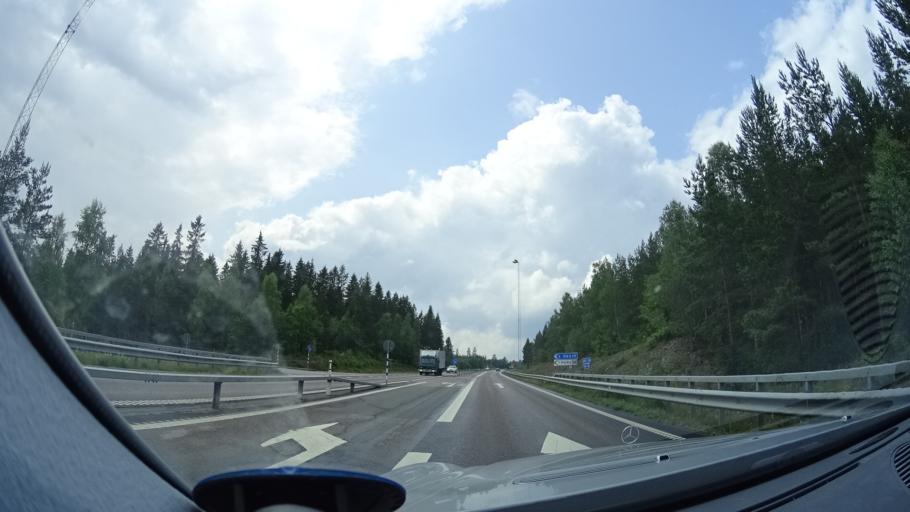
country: SE
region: Kalmar
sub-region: Nybro Kommun
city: Nybro
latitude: 56.7072
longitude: 15.7467
